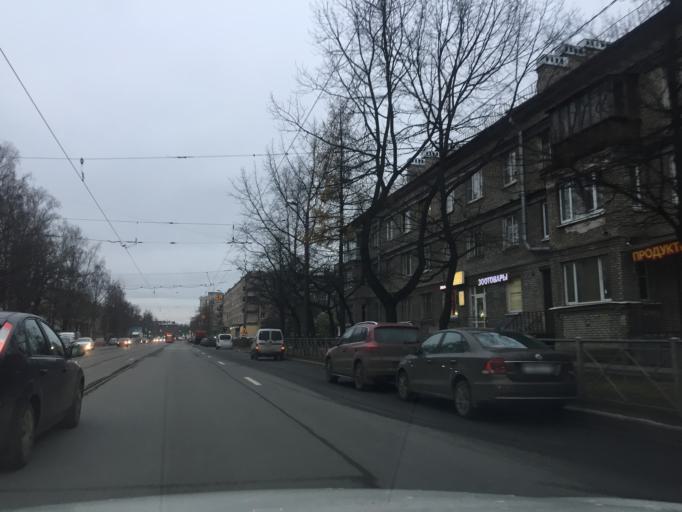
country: RU
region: St.-Petersburg
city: Sosnovka
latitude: 60.0161
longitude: 30.3677
